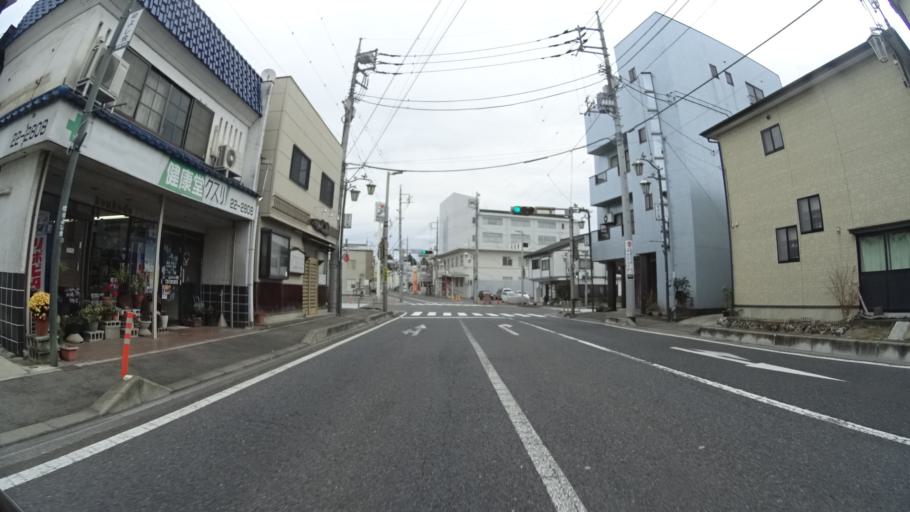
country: JP
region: Gunma
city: Numata
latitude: 36.6445
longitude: 139.0413
